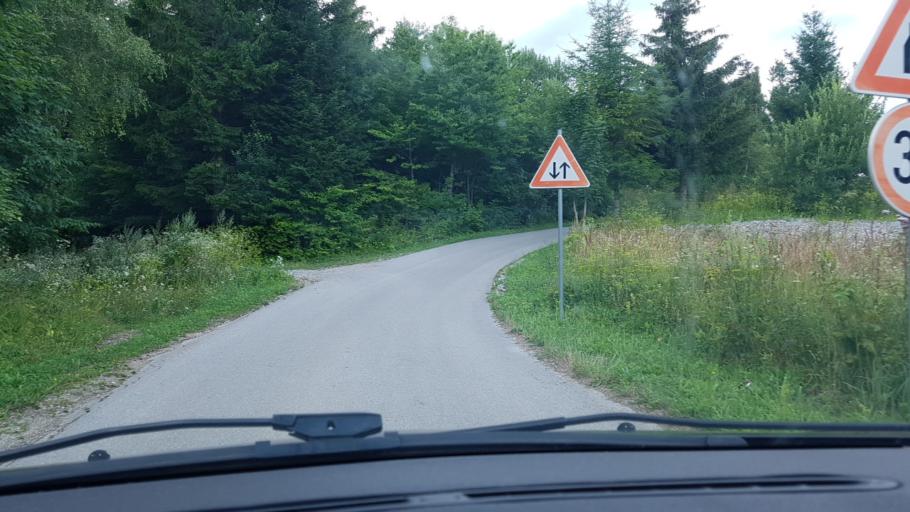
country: HR
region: Primorsko-Goranska
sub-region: Grad Delnice
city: Delnice
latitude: 45.3706
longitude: 14.7083
